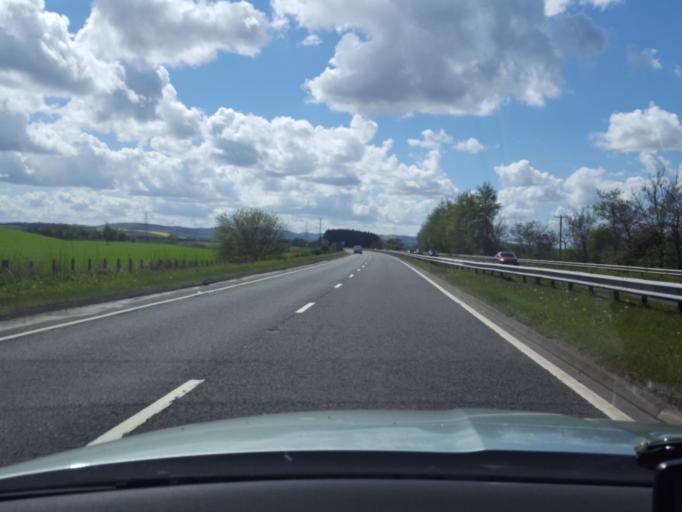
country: GB
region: Scotland
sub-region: Angus
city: Forfar
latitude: 56.6665
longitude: -2.9078
